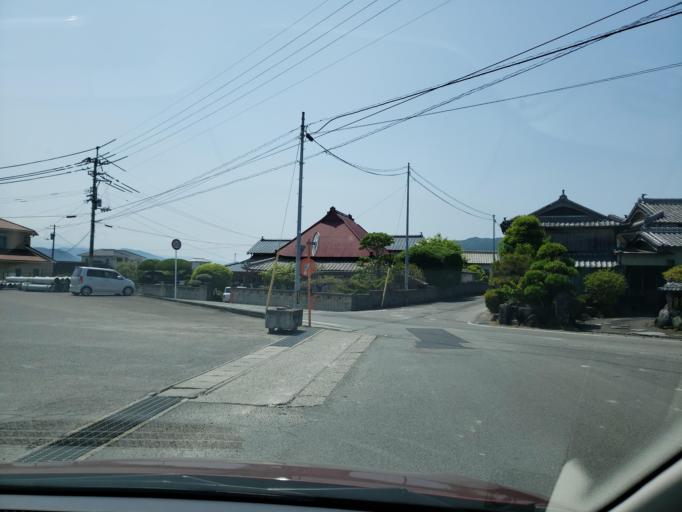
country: JP
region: Tokushima
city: Kamojimacho-jogejima
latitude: 34.0991
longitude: 134.2683
